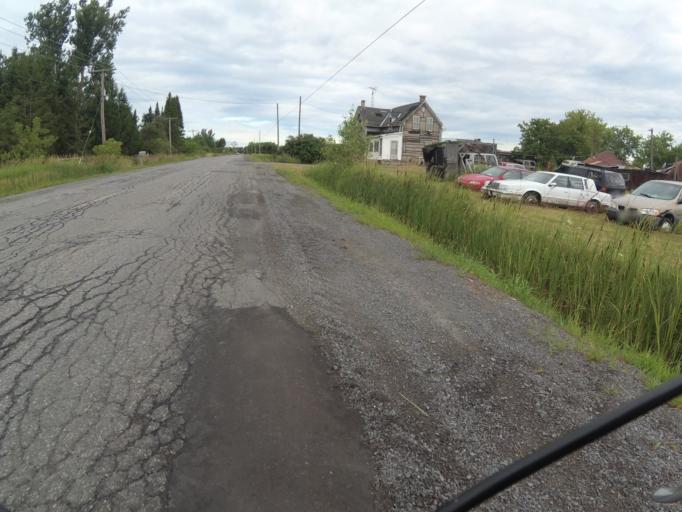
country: CA
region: Ontario
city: Bourget
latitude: 45.3825
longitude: -75.2742
